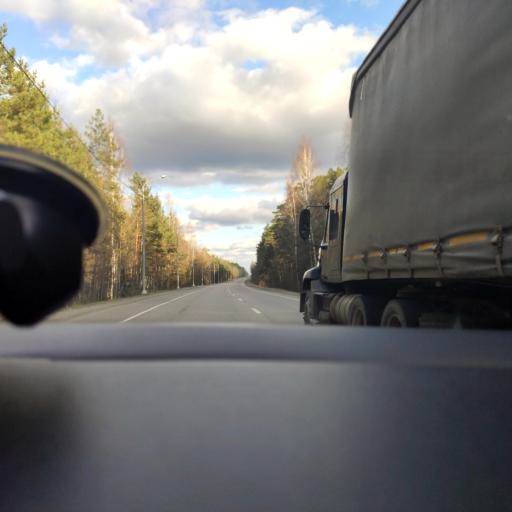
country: RU
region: Moskovskaya
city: Il'inskiy Pogost
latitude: 55.4745
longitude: 38.9538
